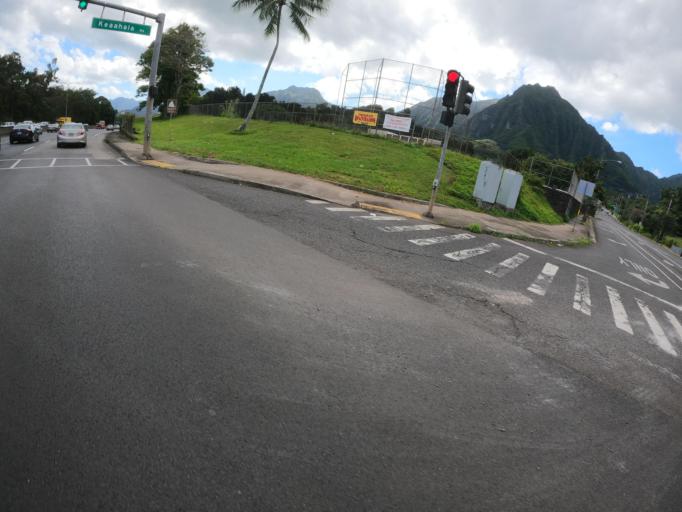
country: US
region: Hawaii
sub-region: Honolulu County
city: Kane'ohe
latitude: 21.4107
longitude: -157.8082
